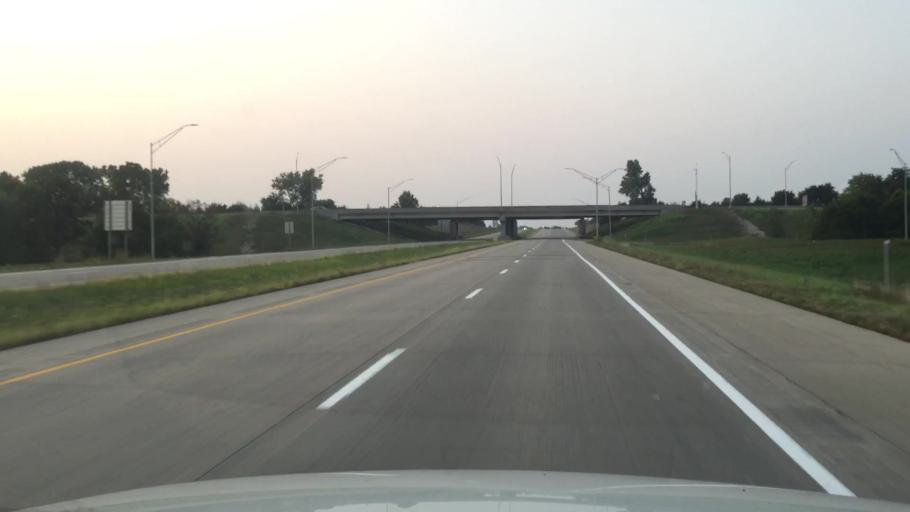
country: US
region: Iowa
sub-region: Clarke County
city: Osceola
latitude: 41.0249
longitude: -93.7942
